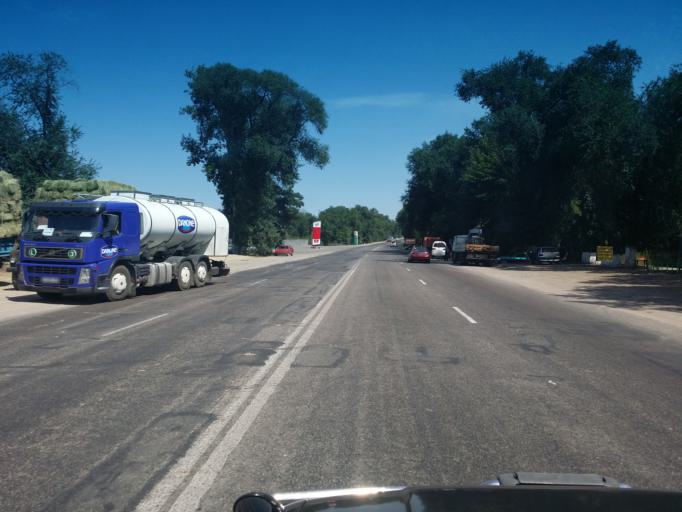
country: KZ
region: Almaty Oblysy
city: Talghar
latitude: 43.4023
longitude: 77.1867
